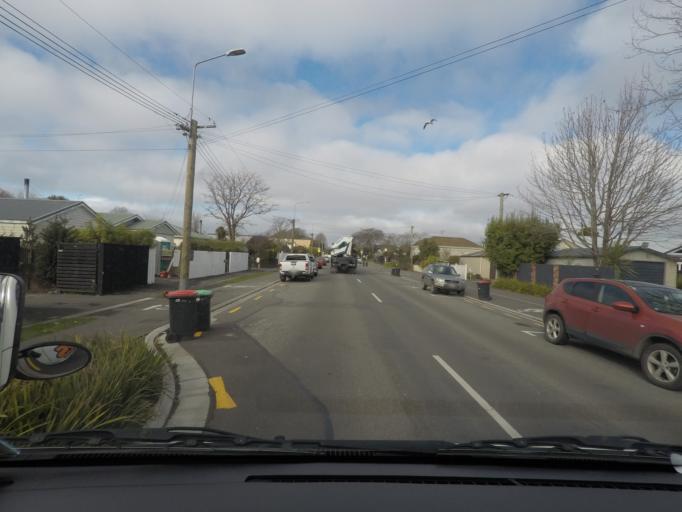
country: NZ
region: Canterbury
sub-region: Christchurch City
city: Christchurch
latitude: -43.5073
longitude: 172.6295
